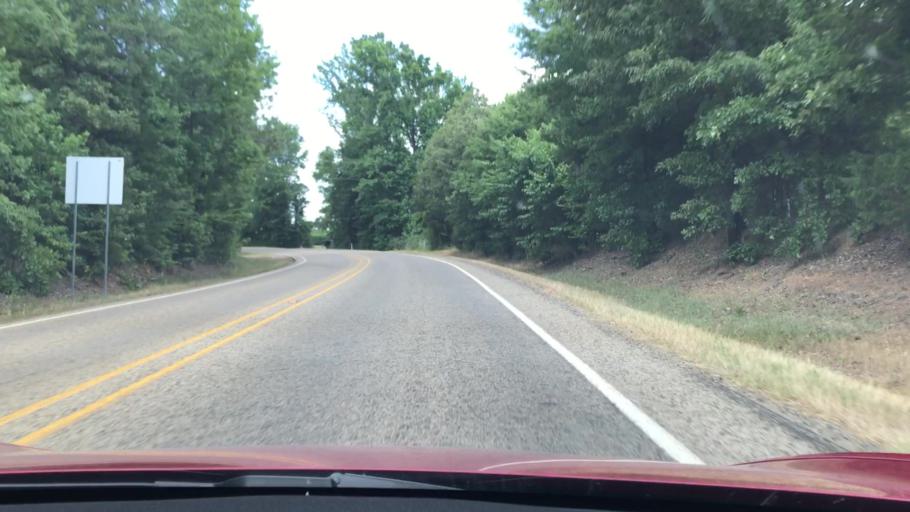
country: US
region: Texas
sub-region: Smith County
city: Hideaway
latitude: 32.4739
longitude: -95.4462
